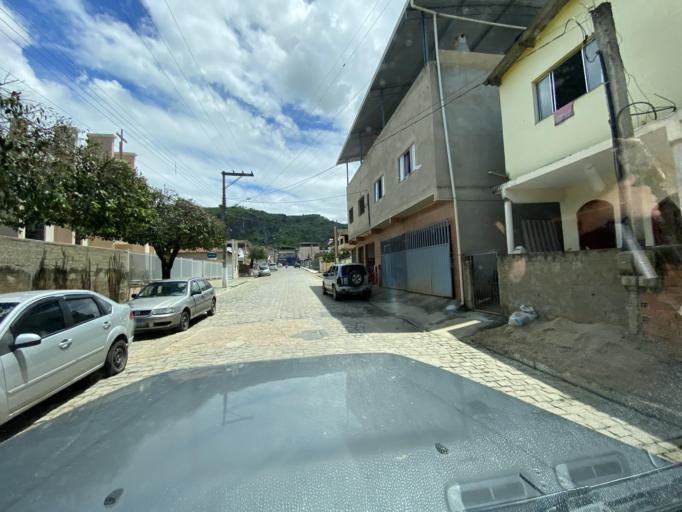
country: BR
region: Espirito Santo
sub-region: Jeronimo Monteiro
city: Jeronimo Monteiro
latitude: -20.7870
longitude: -41.3906
